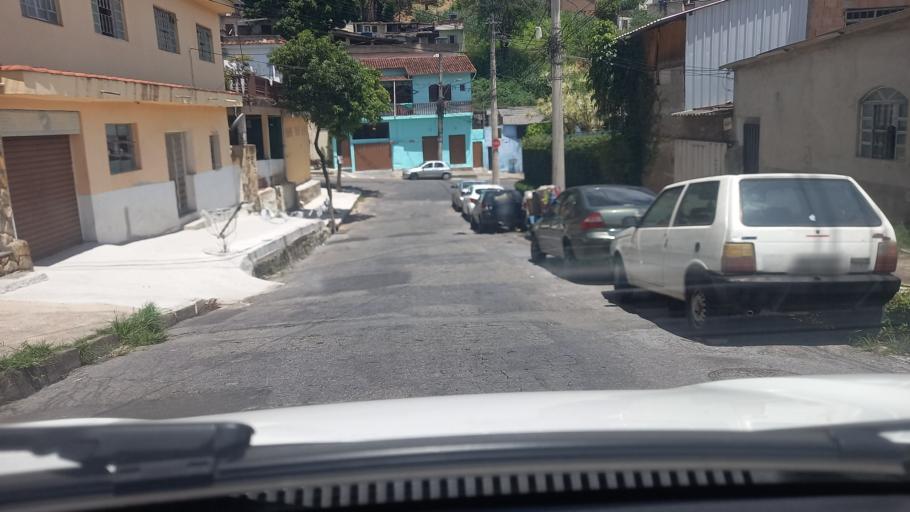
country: BR
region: Minas Gerais
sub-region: Belo Horizonte
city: Belo Horizonte
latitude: -19.9169
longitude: -43.9835
